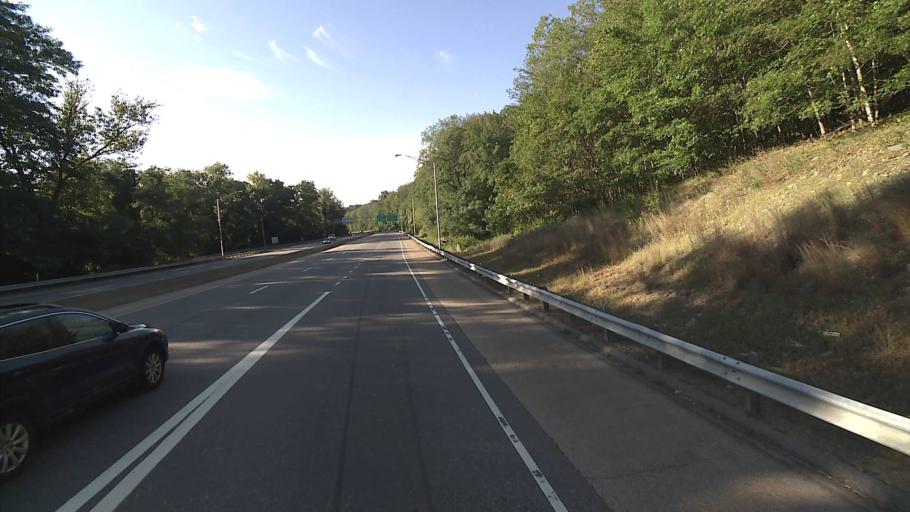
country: US
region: Connecticut
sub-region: New London County
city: Norwich
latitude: 41.5538
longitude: -72.1177
